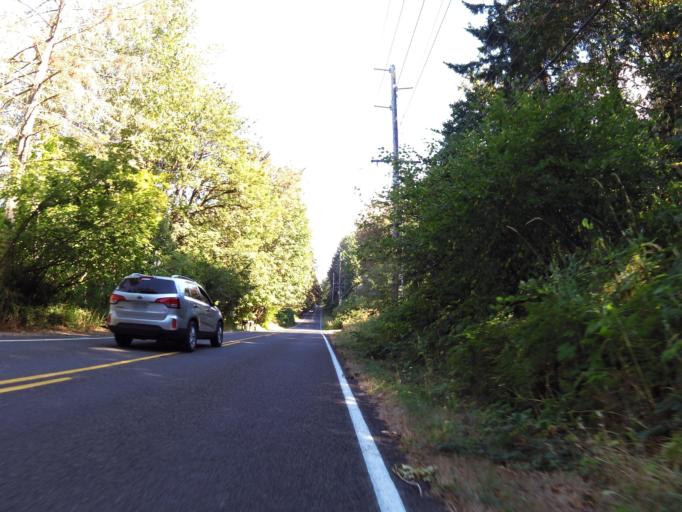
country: US
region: Washington
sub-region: Thurston County
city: Olympia
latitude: 47.0574
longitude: -123.0113
